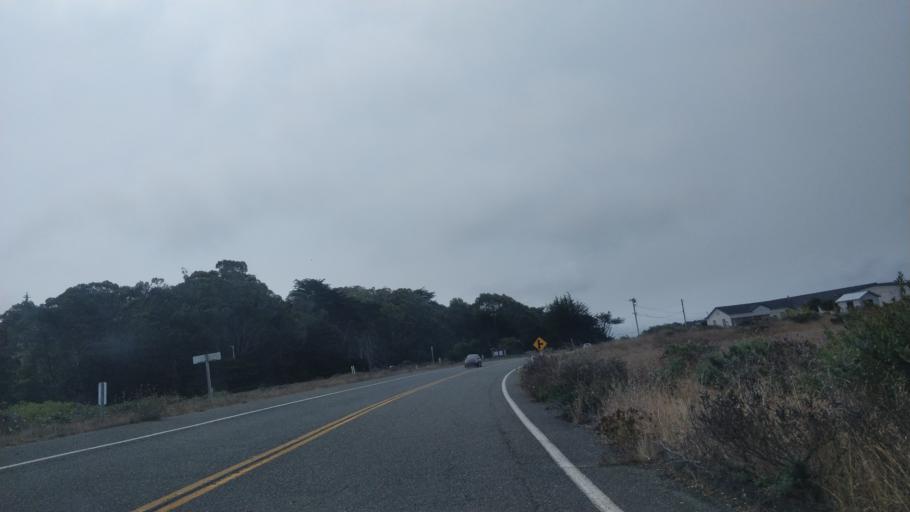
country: US
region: California
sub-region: Humboldt County
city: Bayview
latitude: 40.7810
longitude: -124.2070
